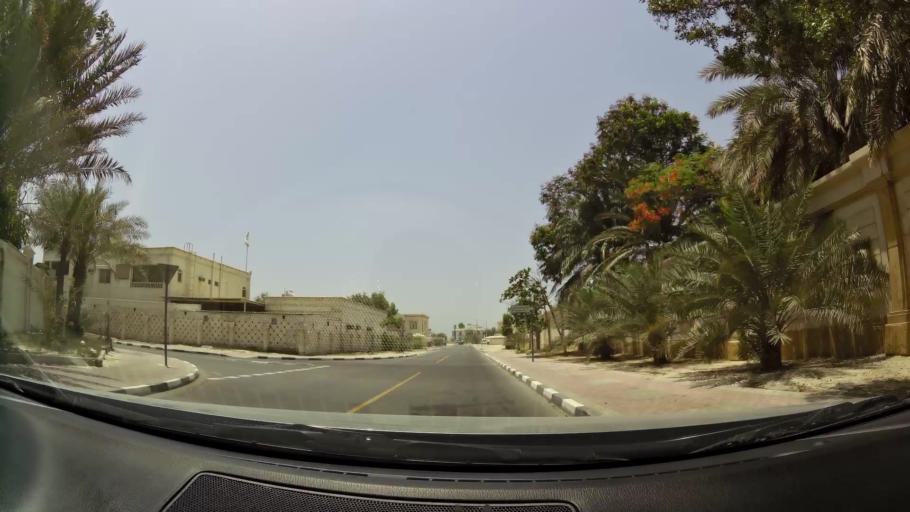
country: AE
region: Dubai
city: Dubai
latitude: 25.1542
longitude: 55.2062
